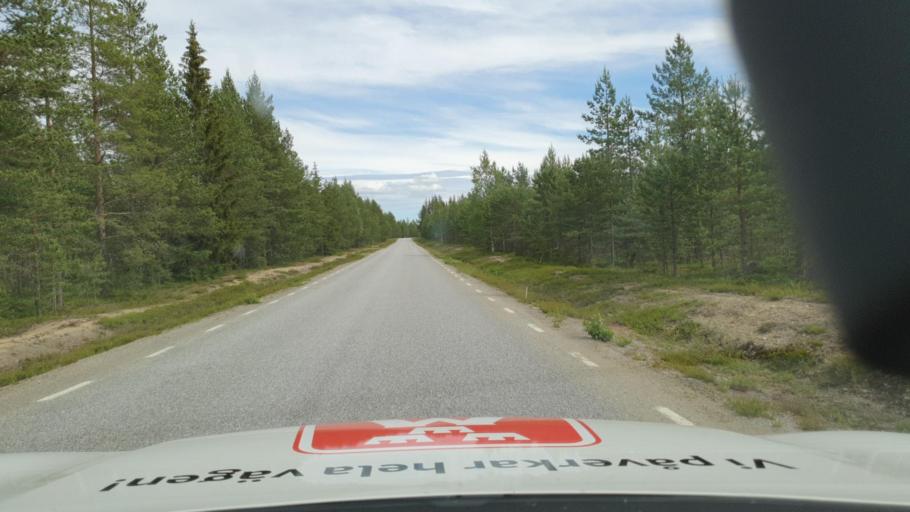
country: SE
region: Vaesterbotten
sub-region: Skelleftea Kommun
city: Burtraesk
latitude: 64.5034
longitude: 20.8253
